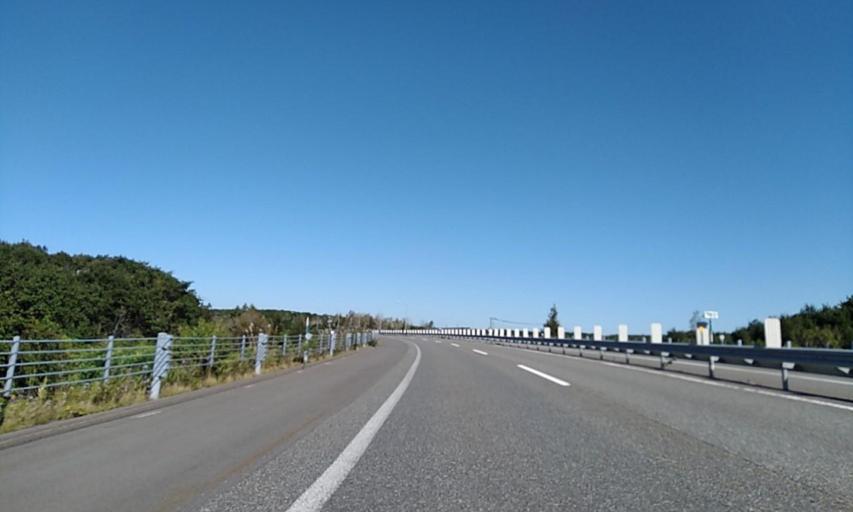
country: JP
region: Hokkaido
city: Tomakomai
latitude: 42.6527
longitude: 141.8307
